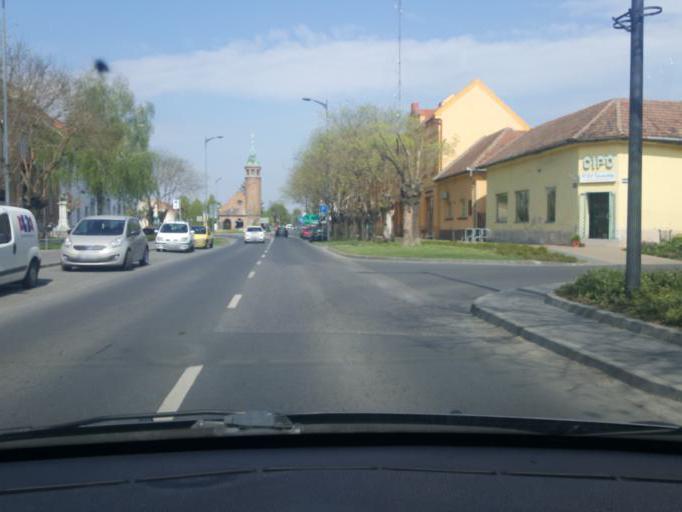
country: HU
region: Pest
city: Monor
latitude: 47.3511
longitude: 19.4460
